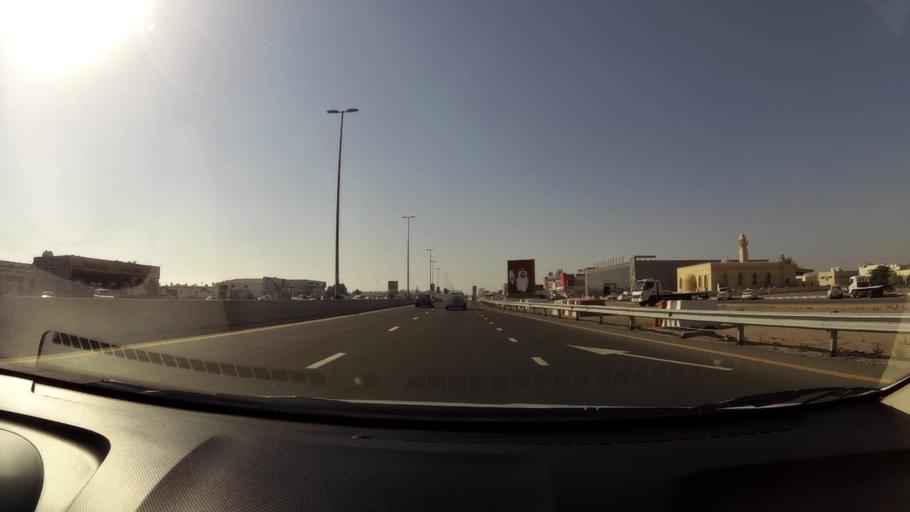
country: AE
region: Umm al Qaywayn
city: Umm al Qaywayn
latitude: 25.5005
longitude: 55.5506
